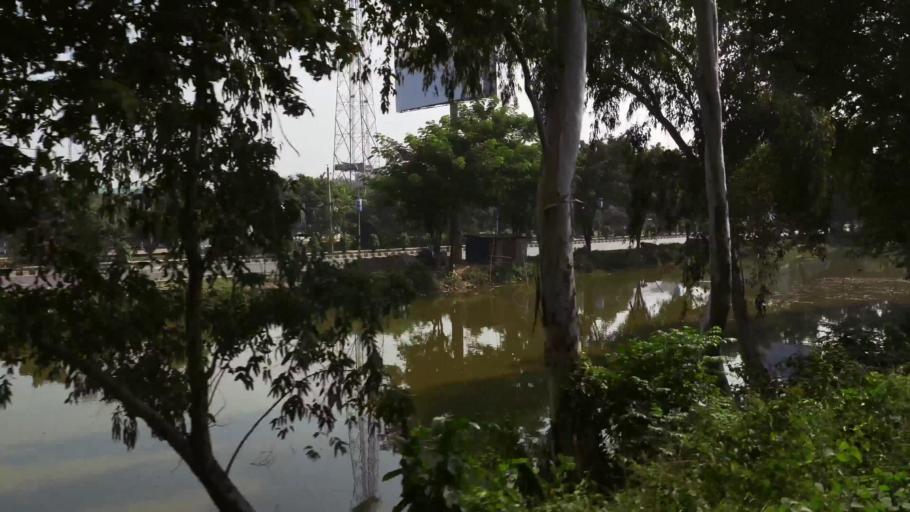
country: BD
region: Dhaka
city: Tungi
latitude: 23.8385
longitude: 90.4184
